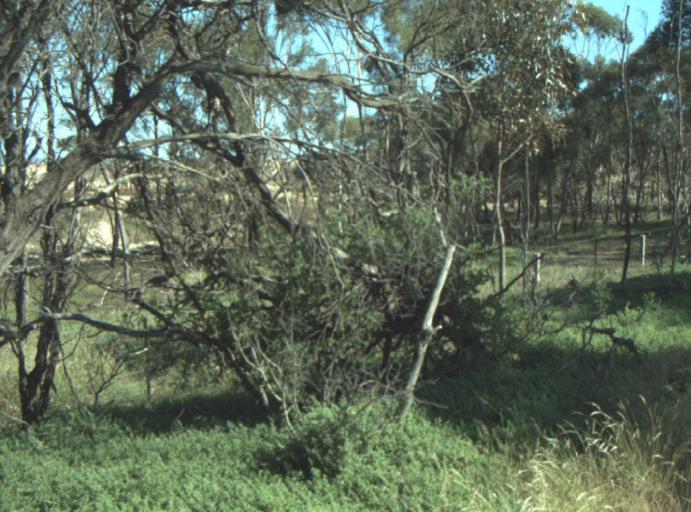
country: AU
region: Victoria
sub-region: Greater Geelong
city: Lara
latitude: -37.9242
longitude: 144.3958
